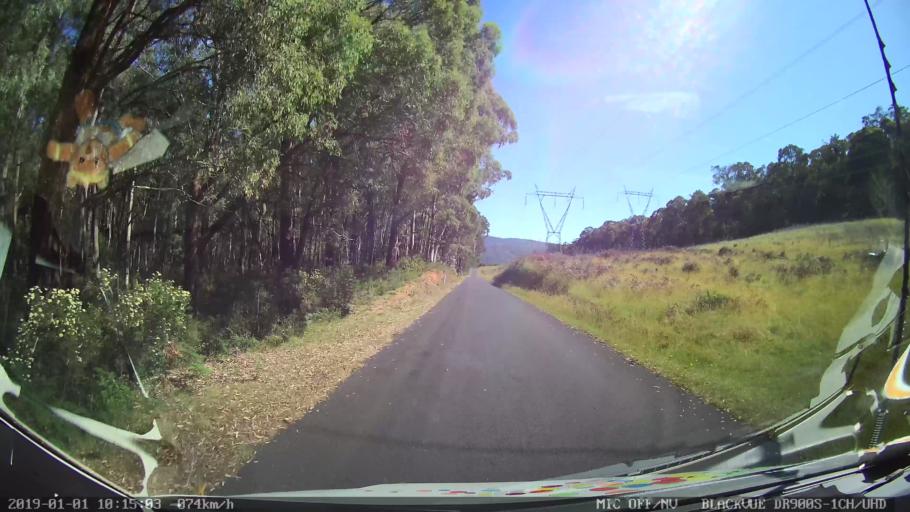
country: AU
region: New South Wales
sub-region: Snowy River
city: Jindabyne
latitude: -36.1059
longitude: 148.1617
